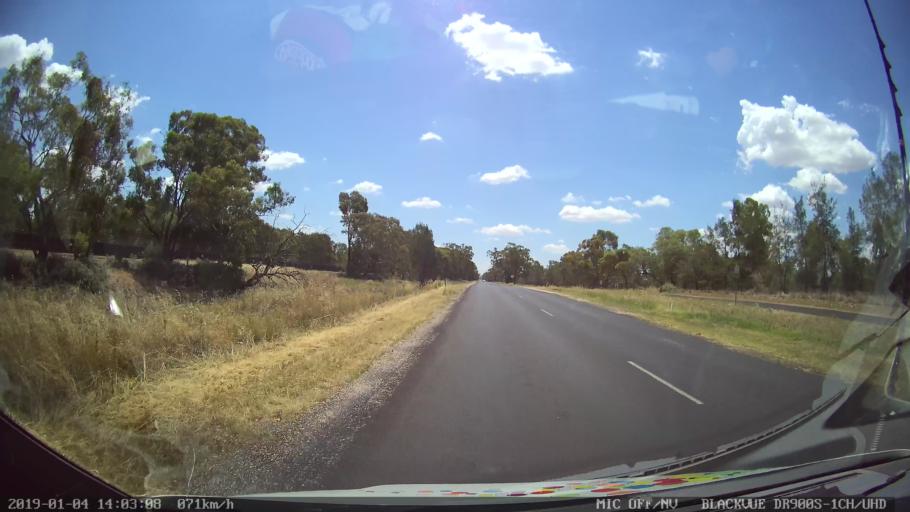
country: AU
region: New South Wales
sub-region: Dubbo Municipality
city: Dubbo
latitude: -32.2801
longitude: 148.5933
